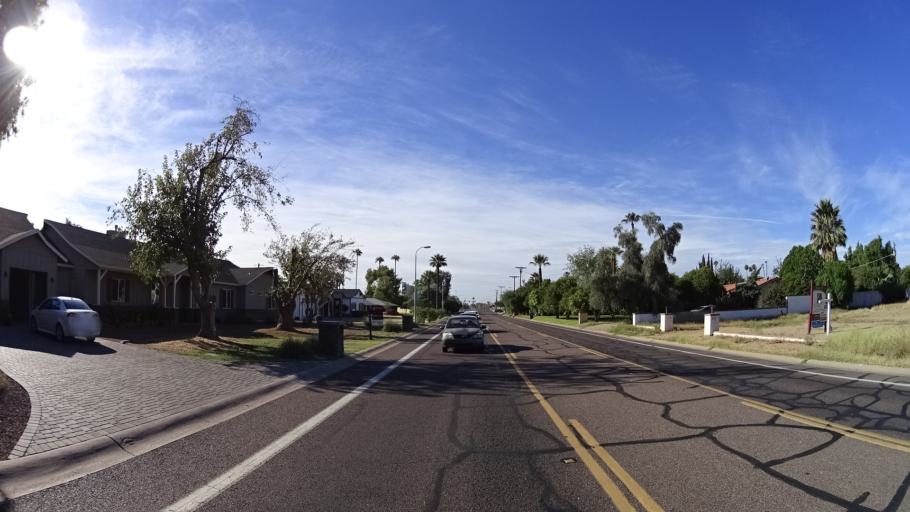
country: US
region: Arizona
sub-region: Maricopa County
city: Paradise Valley
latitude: 33.4976
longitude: -111.9346
